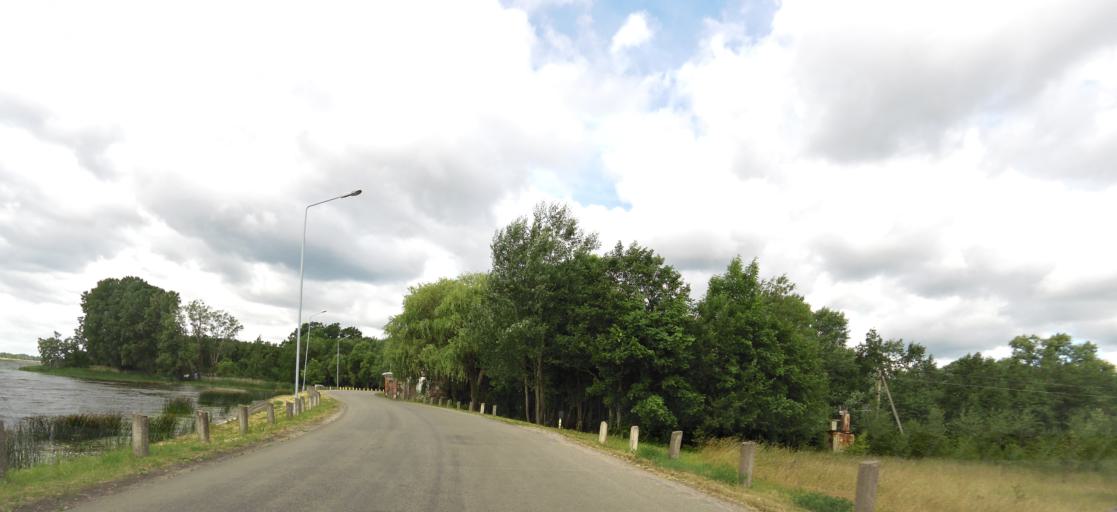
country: LT
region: Panevezys
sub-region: Birzai
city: Birzai
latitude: 56.2219
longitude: 24.7599
